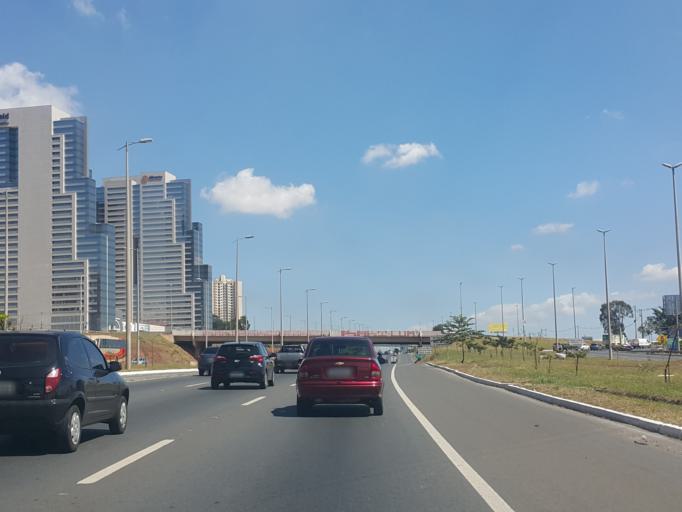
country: BR
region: Federal District
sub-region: Brasilia
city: Brasilia
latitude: -15.8298
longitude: -48.0368
